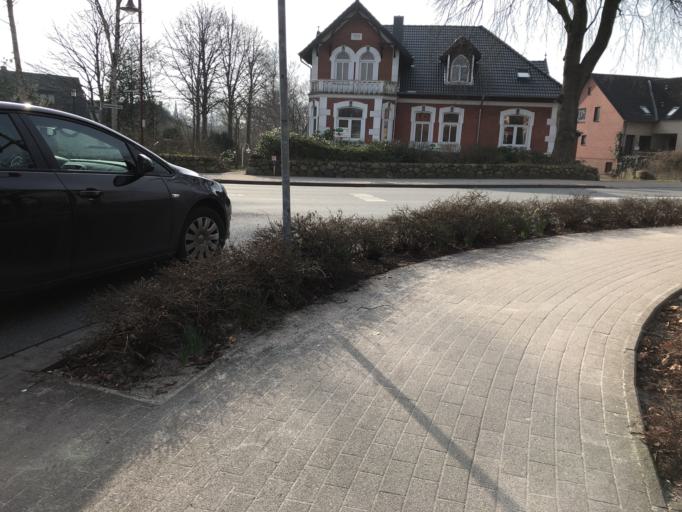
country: DE
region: Schleswig-Holstein
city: Tarp
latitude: 54.6642
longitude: 9.4003
